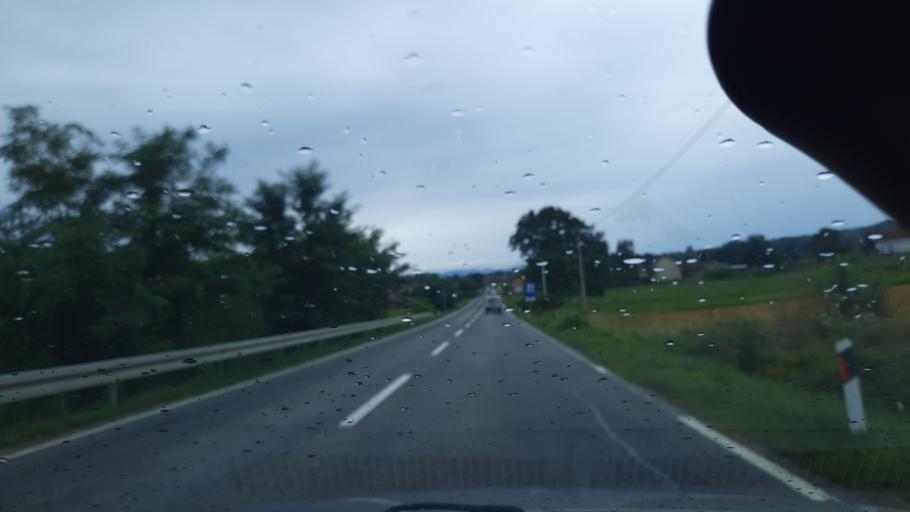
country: RS
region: Central Serbia
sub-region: Raski Okrug
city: Kraljevo
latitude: 43.7882
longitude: 20.7908
